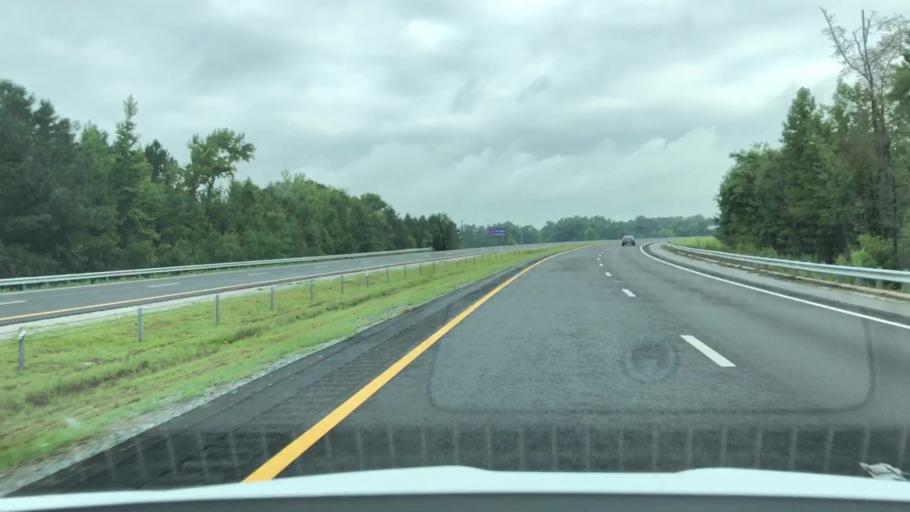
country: US
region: North Carolina
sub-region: Wayne County
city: Fremont
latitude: 35.5058
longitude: -77.9998
